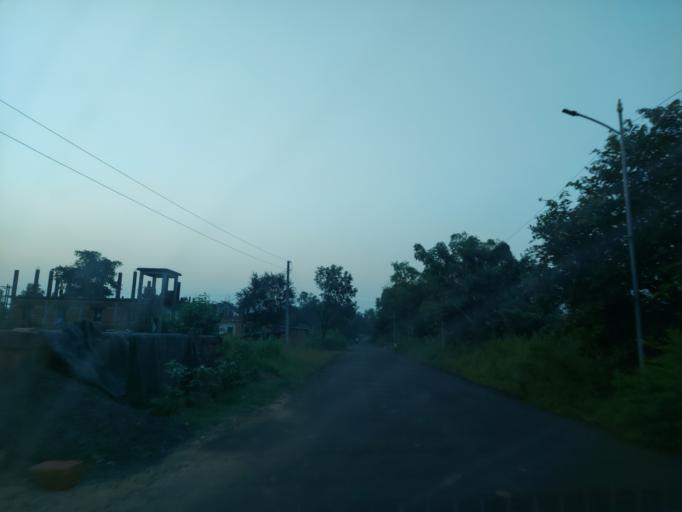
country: IN
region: Maharashtra
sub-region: Sindhudurg
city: Kudal
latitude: 16.1043
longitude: 73.7066
